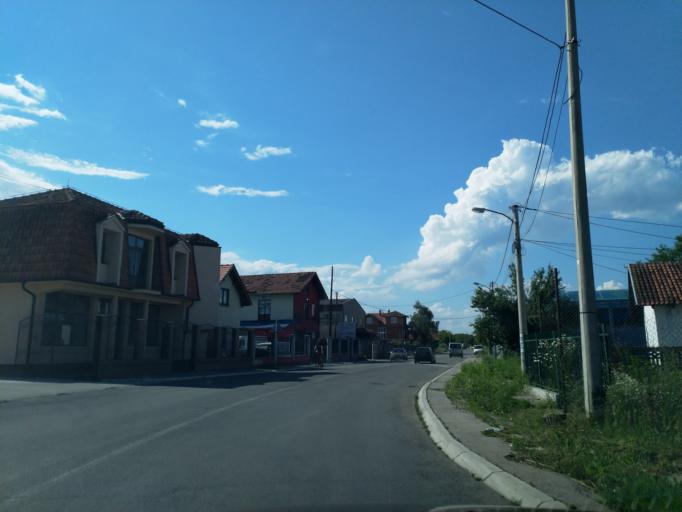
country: RS
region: Central Serbia
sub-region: Pomoravski Okrug
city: Paracin
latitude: 43.8471
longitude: 21.4128
